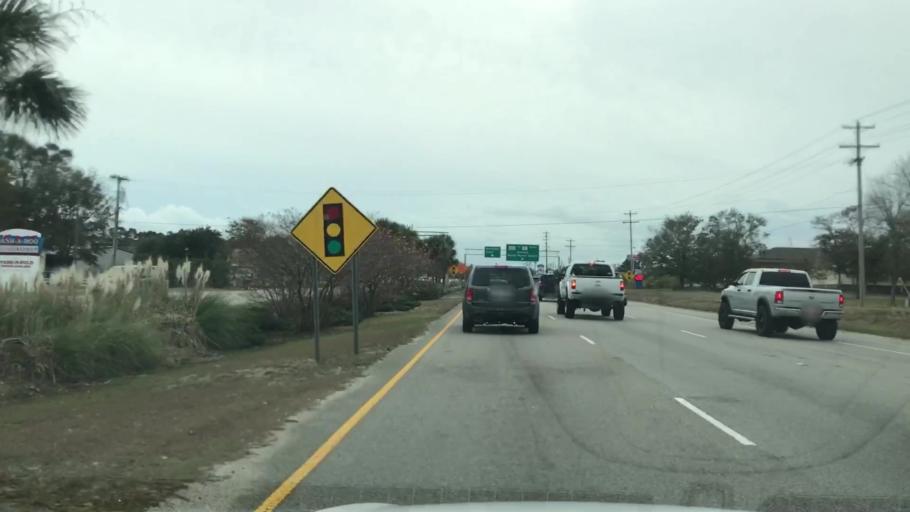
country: US
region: South Carolina
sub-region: Georgetown County
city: Murrells Inlet
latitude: 33.5695
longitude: -79.0327
